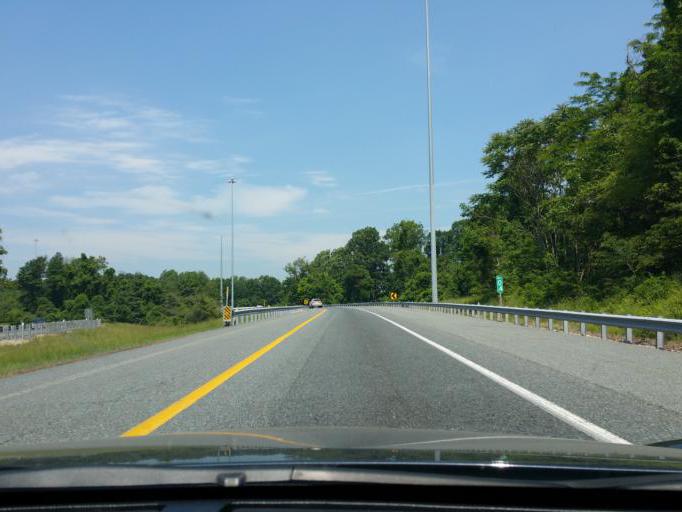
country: US
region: Maryland
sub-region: Howard County
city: Elkridge
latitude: 39.2219
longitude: -76.7173
